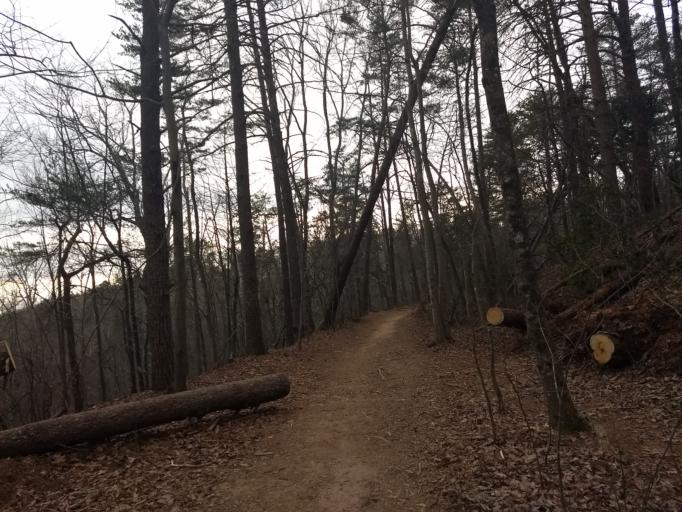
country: US
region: South Carolina
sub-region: Greenville County
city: Travelers Rest
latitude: 34.9449
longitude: -82.3958
